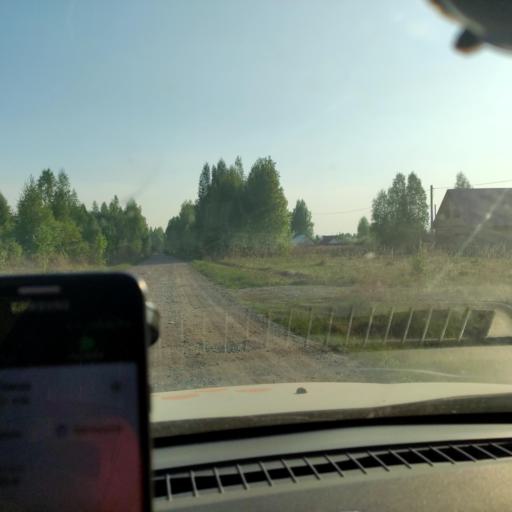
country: RU
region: Bashkortostan
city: Kabakovo
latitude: 54.7284
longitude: 56.2309
